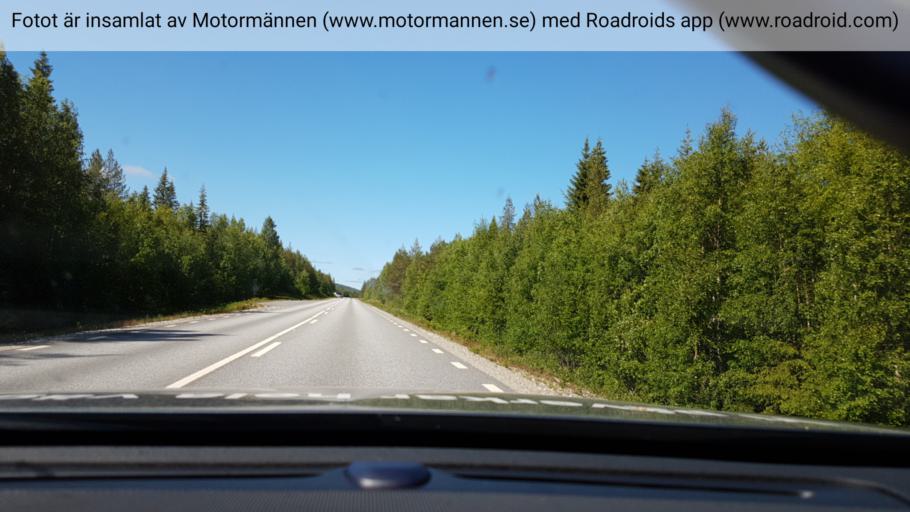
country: SE
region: Vaesterbotten
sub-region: Asele Kommun
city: Insjon
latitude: 64.2004
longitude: 17.6388
